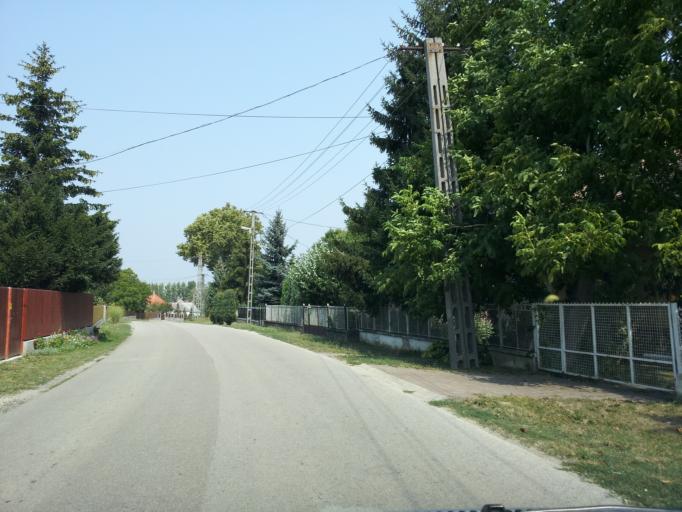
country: HU
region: Gyor-Moson-Sopron
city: Bakonyszentlaszlo
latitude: 47.3921
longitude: 17.8036
